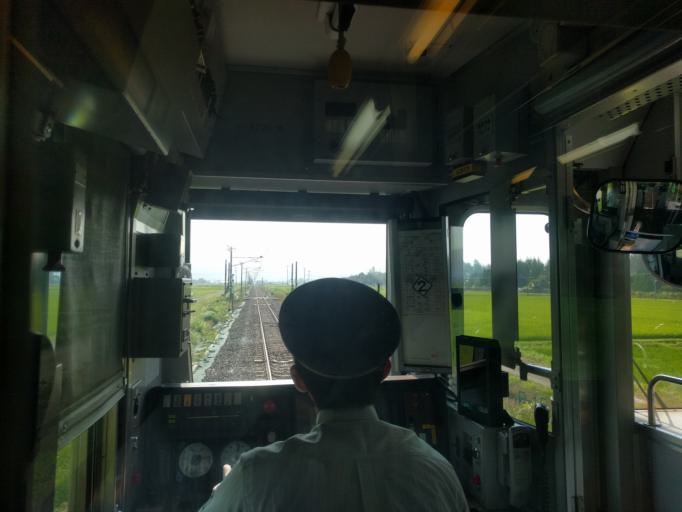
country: JP
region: Fukushima
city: Inawashiro
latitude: 37.5493
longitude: 140.0809
